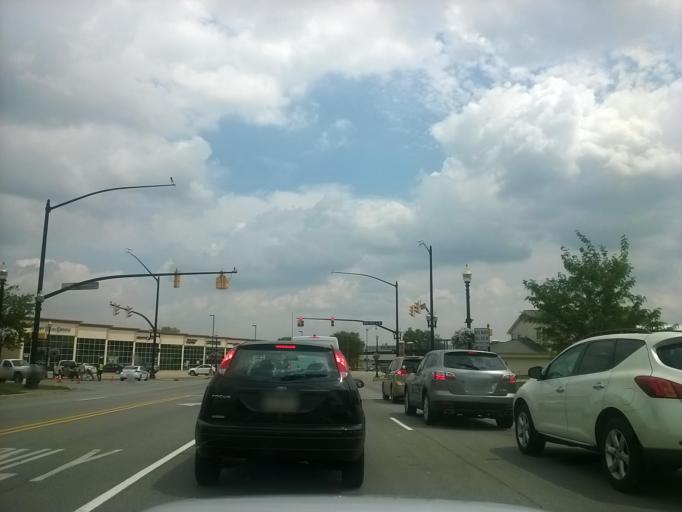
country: US
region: Indiana
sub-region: Hamilton County
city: Carmel
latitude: 39.9623
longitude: -86.1329
